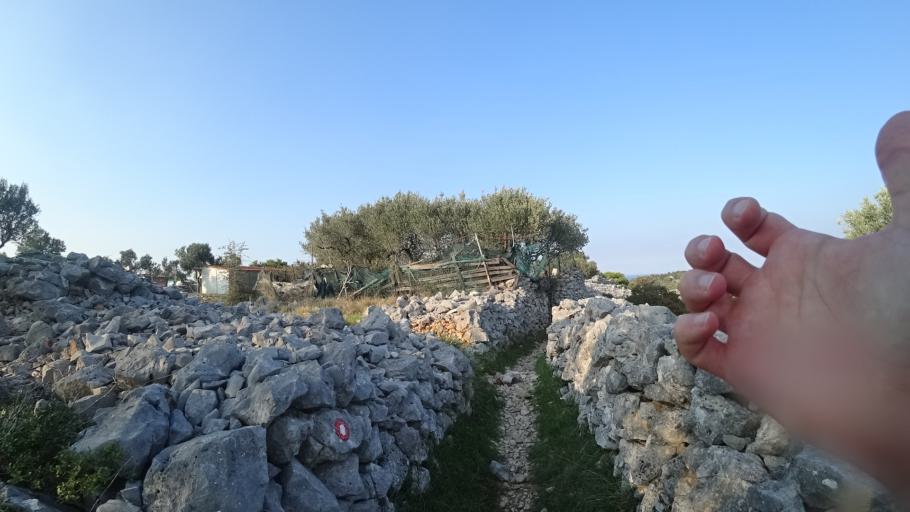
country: HR
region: Primorsko-Goranska
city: Mali Losinj
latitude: 44.5255
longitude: 14.4758
